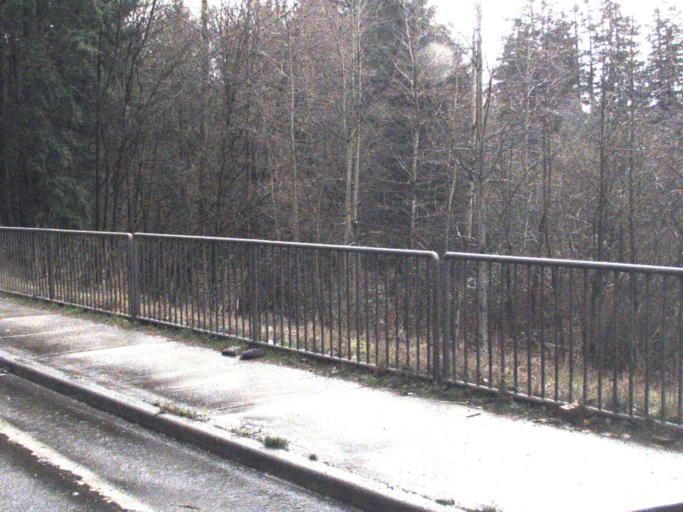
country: US
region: Washington
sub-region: Snohomish County
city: Mill Creek
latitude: 47.8799
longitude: -122.2191
